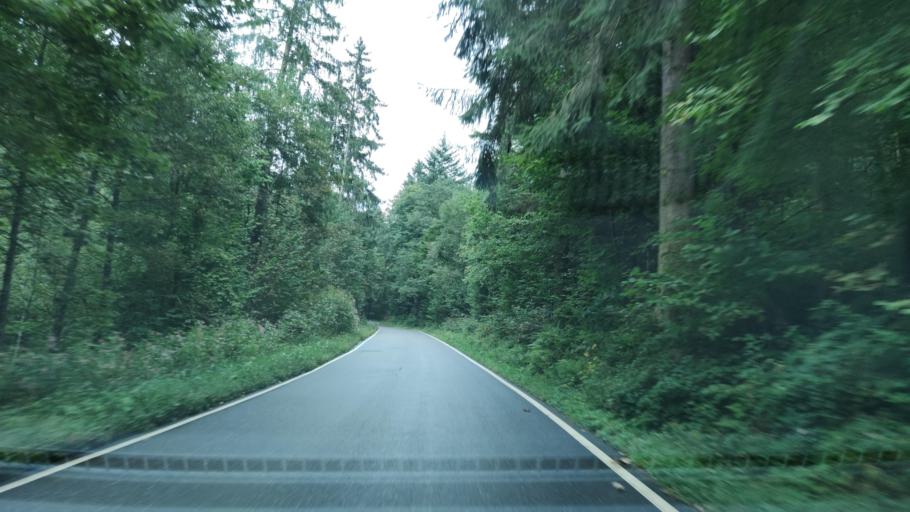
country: DE
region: Baden-Wuerttemberg
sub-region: Freiburg Region
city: Sasbachwalden
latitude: 48.6326
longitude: 8.1685
